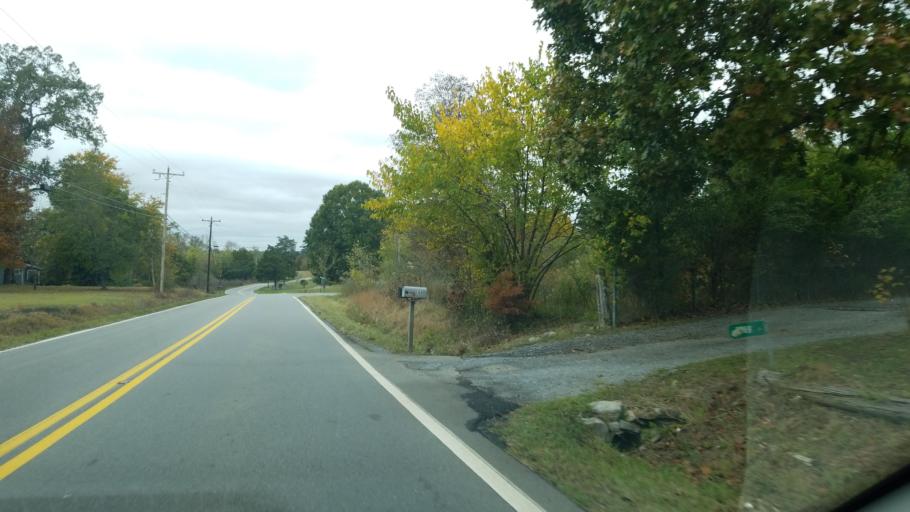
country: US
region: Tennessee
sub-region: Hamilton County
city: Sale Creek
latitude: 35.3717
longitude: -84.9951
